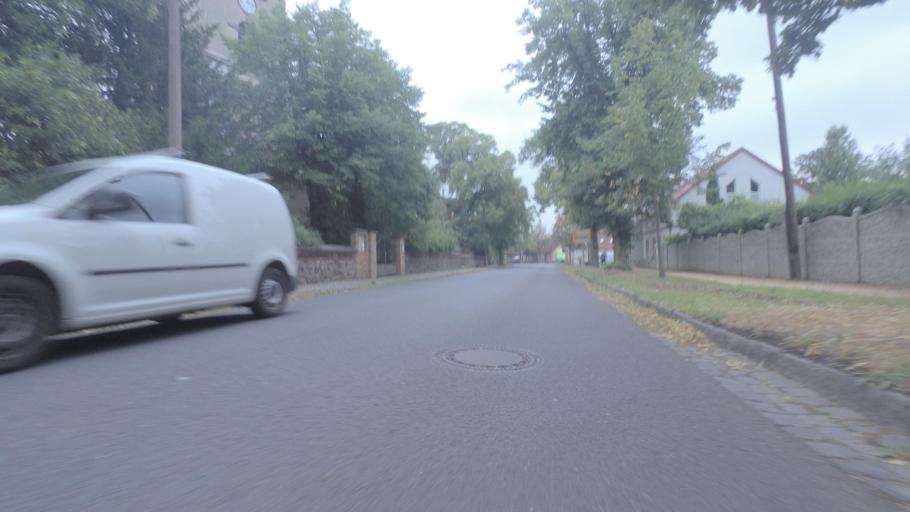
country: DE
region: Brandenburg
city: Potsdam
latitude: 52.4678
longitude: 13.0137
